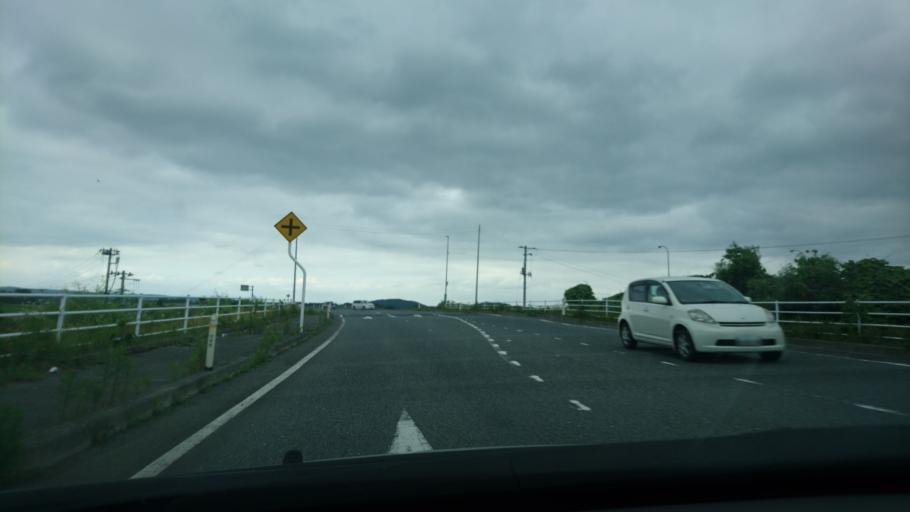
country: JP
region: Miyagi
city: Wakuya
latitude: 38.7306
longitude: 141.1520
